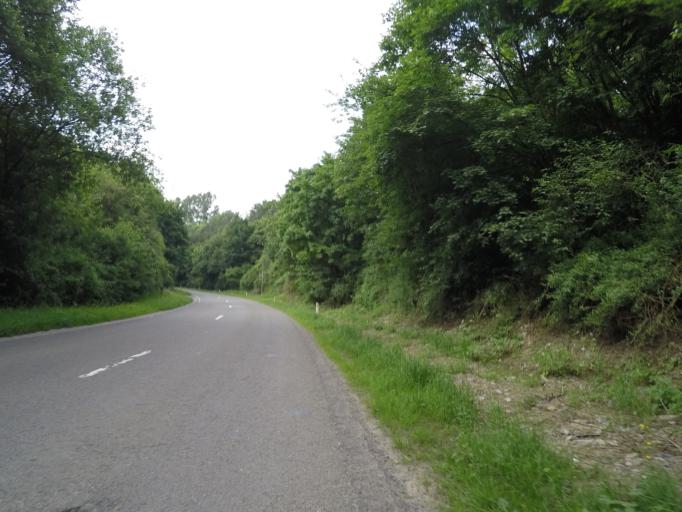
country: BE
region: Wallonia
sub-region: Province de Namur
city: Assesse
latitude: 50.3185
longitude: 5.0249
